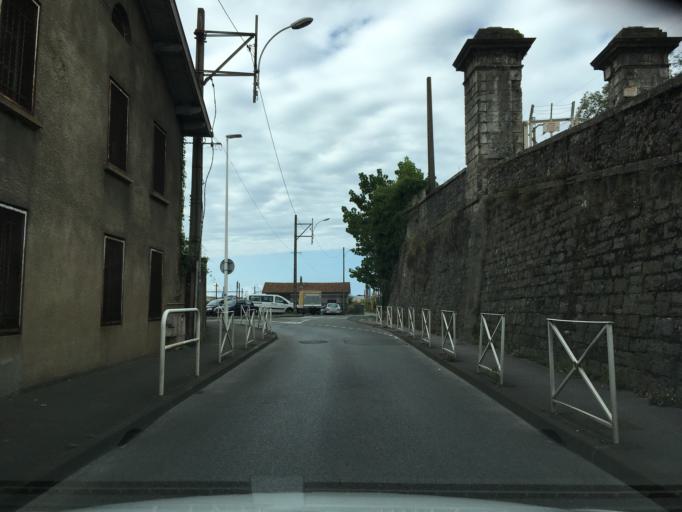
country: FR
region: Aquitaine
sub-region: Departement des Pyrenees-Atlantiques
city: Bayonne
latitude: 43.4968
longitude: -1.4738
